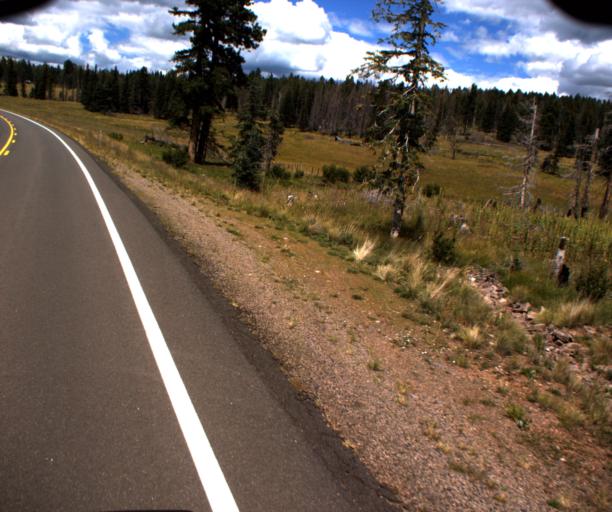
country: US
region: Arizona
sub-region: Apache County
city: Eagar
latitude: 33.9291
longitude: -109.4662
